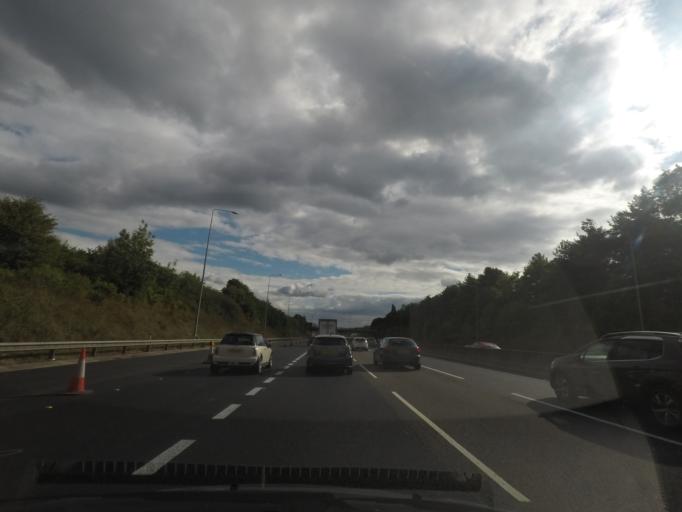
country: GB
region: England
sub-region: Derbyshire
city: Long Eaton
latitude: 52.9228
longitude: -1.2999
